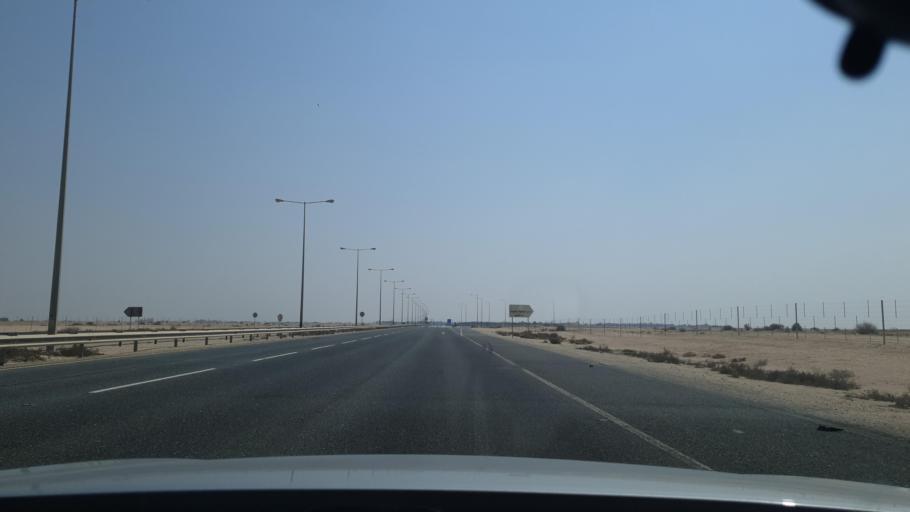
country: QA
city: Al Ghuwayriyah
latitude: 25.8001
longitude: 51.3832
